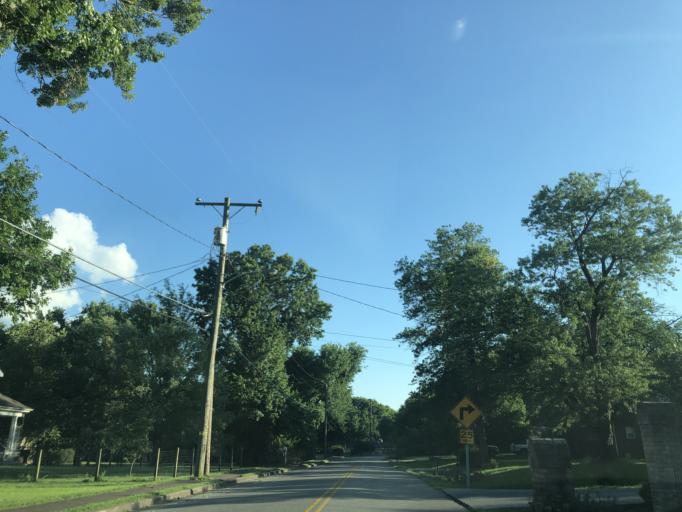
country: US
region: Tennessee
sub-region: Davidson County
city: Nashville
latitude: 36.1880
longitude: -86.8322
